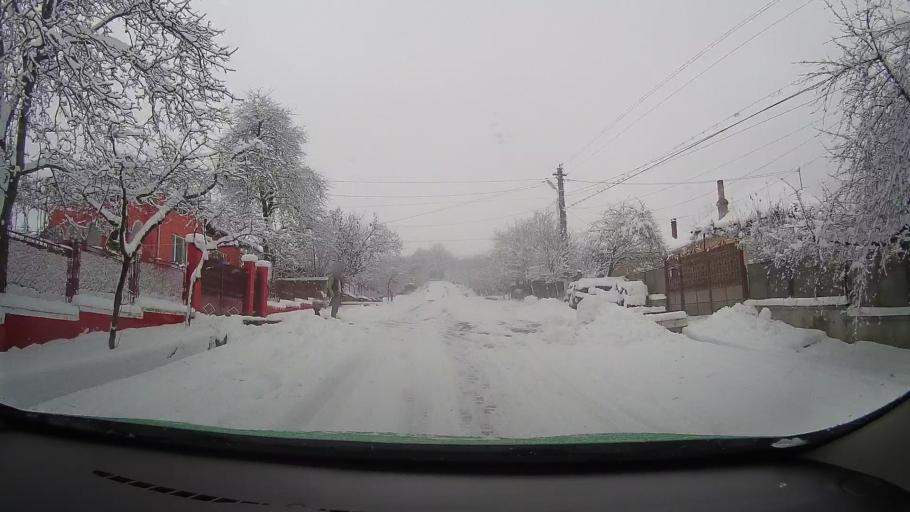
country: RO
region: Hunedoara
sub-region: Comuna Teliucu Inferior
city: Teliucu Inferior
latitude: 45.7000
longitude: 22.8922
